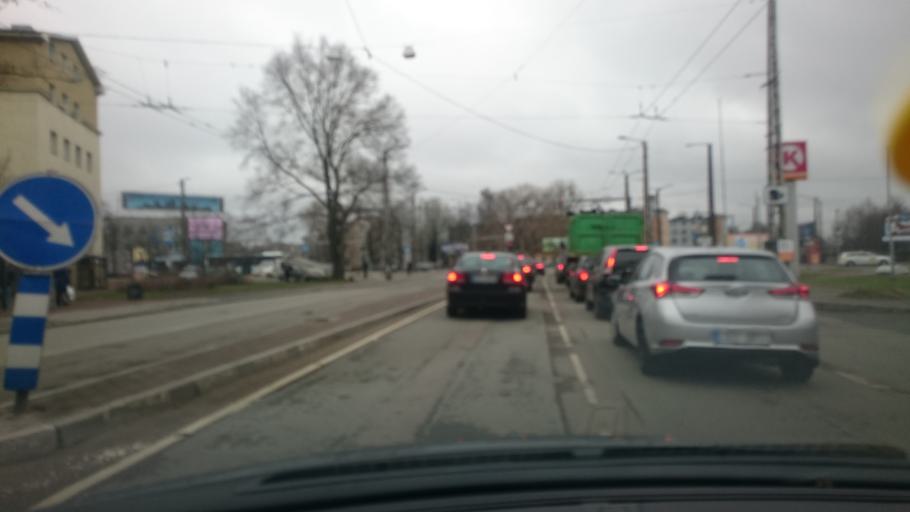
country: EE
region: Harju
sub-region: Tallinna linn
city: Tallinn
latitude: 59.4282
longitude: 24.7201
